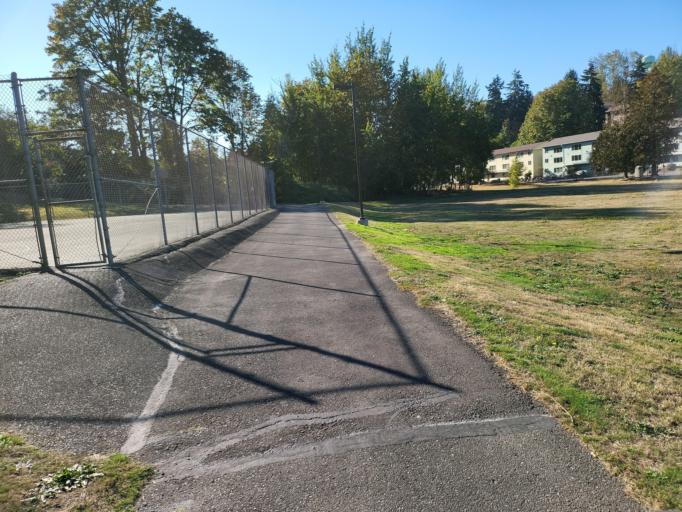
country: US
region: Washington
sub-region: King County
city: Bryn Mawr-Skyway
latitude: 47.4913
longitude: -122.2442
